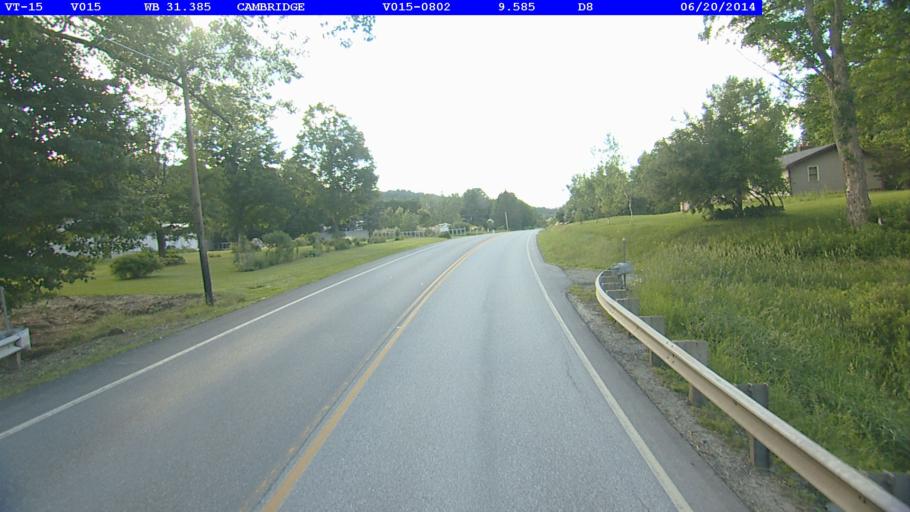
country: US
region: Vermont
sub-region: Lamoille County
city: Johnson
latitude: 44.6513
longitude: -72.7594
